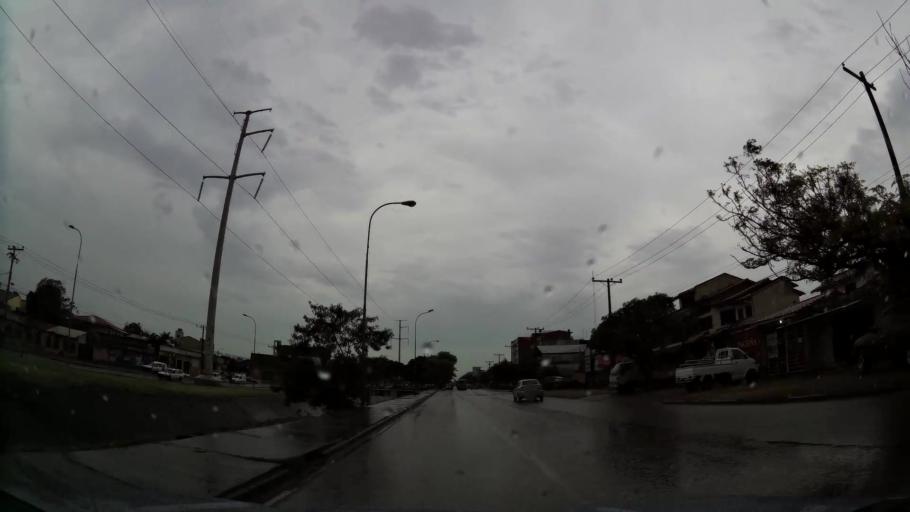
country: BO
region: Santa Cruz
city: Santa Cruz de la Sierra
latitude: -17.7835
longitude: -63.1480
